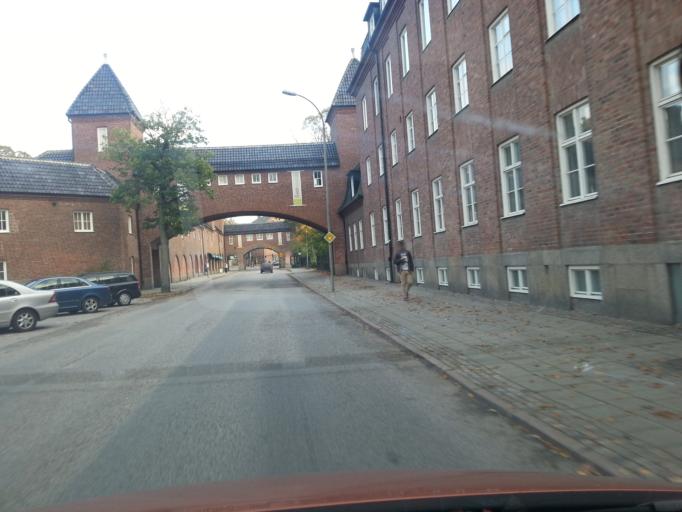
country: SE
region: Skane
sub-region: Lunds Kommun
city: Lund
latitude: 55.7088
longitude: 13.1945
